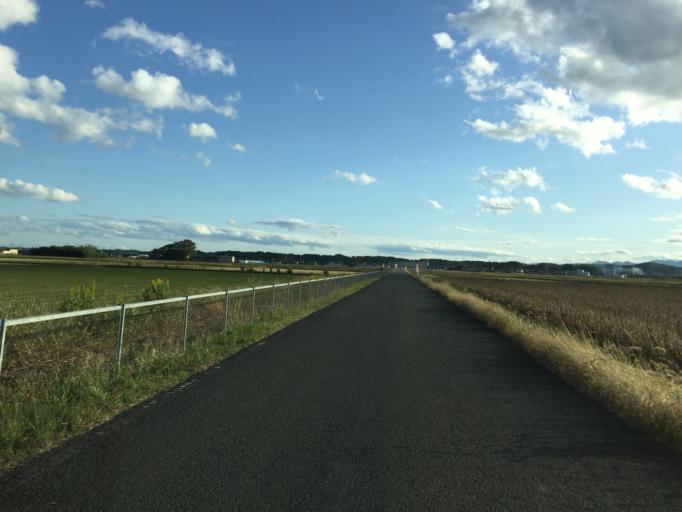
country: JP
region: Miyagi
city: Marumori
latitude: 37.7991
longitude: 140.9487
